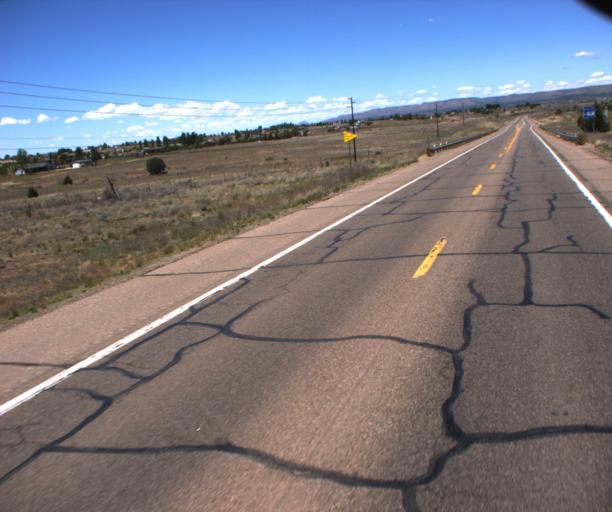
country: US
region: Arizona
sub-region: Yavapai County
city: Paulden
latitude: 34.8566
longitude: -112.4682
